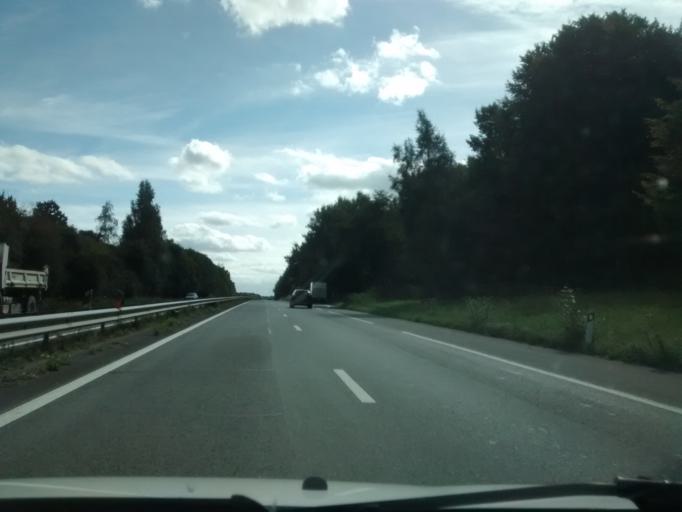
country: FR
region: Brittany
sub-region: Departement d'Ille-et-Vilaine
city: Miniac-Morvan
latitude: 48.5216
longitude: -1.9154
